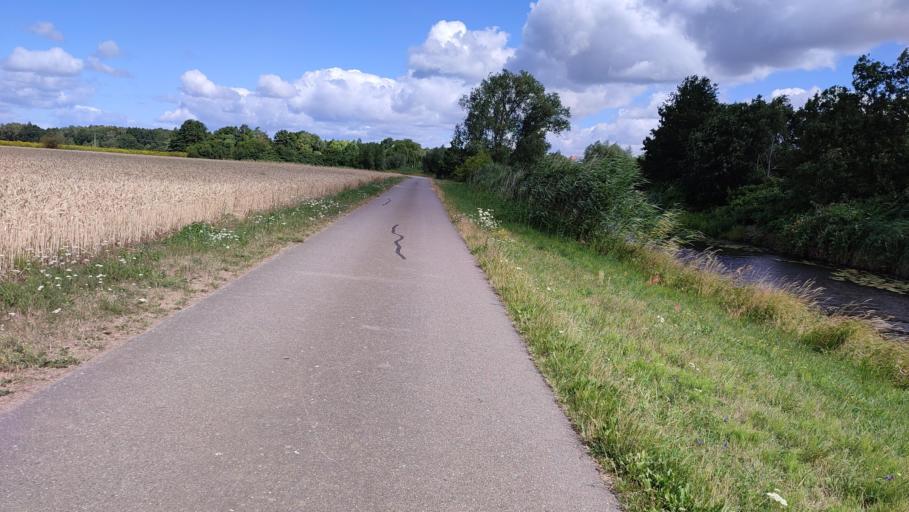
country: DE
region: Lower Saxony
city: Neu Darchau
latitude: 53.2282
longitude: 10.9804
